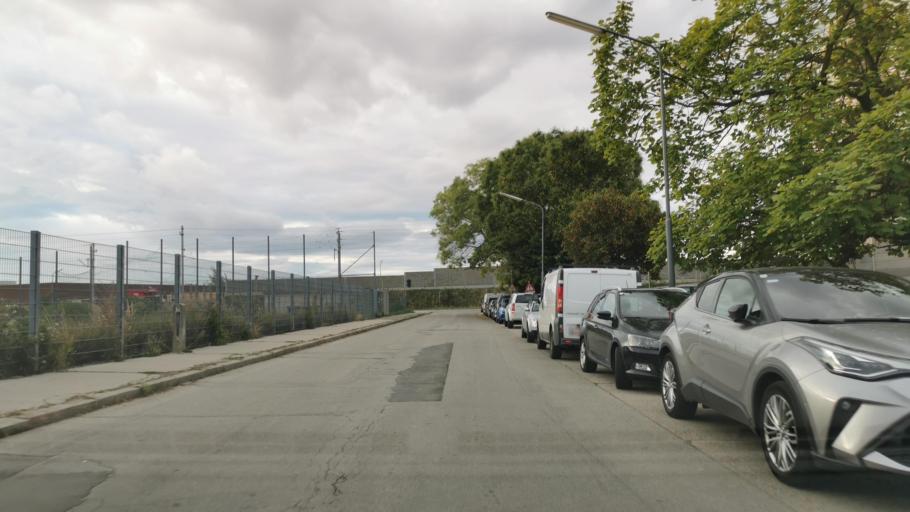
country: AT
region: Lower Austria
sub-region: Politischer Bezirk Wien-Umgebung
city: Gerasdorf bei Wien
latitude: 48.2341
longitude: 16.4723
